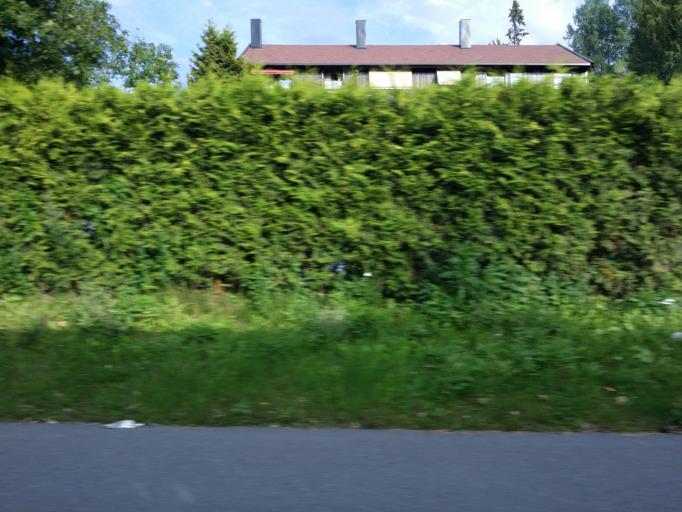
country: NO
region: Akershus
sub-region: Oppegard
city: Kolbotn
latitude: 59.8898
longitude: 10.8537
